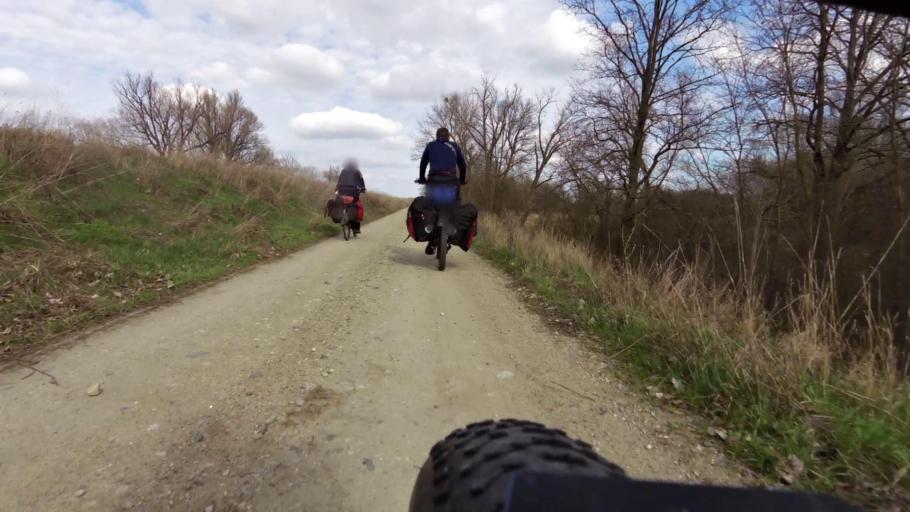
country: DE
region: Brandenburg
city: Lebus
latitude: 52.4357
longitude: 14.5600
